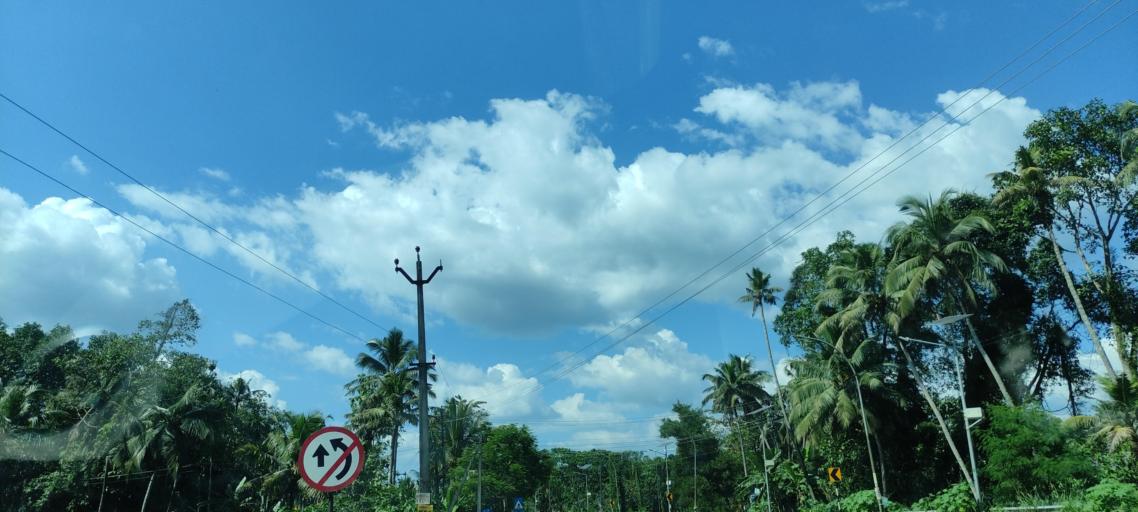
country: IN
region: Kerala
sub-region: Pattanamtitta
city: Adur
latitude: 9.1544
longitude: 76.7272
